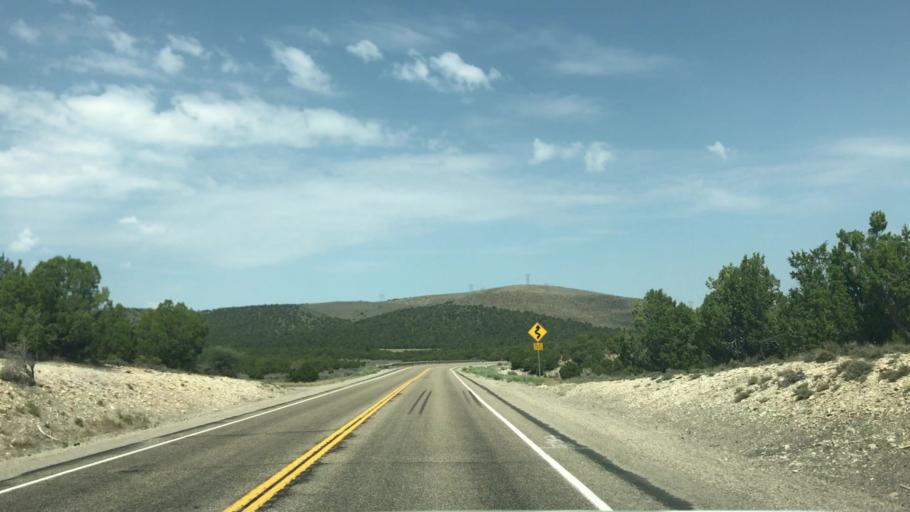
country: US
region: Nevada
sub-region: White Pine County
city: Ely
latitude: 39.3903
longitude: -115.0792
